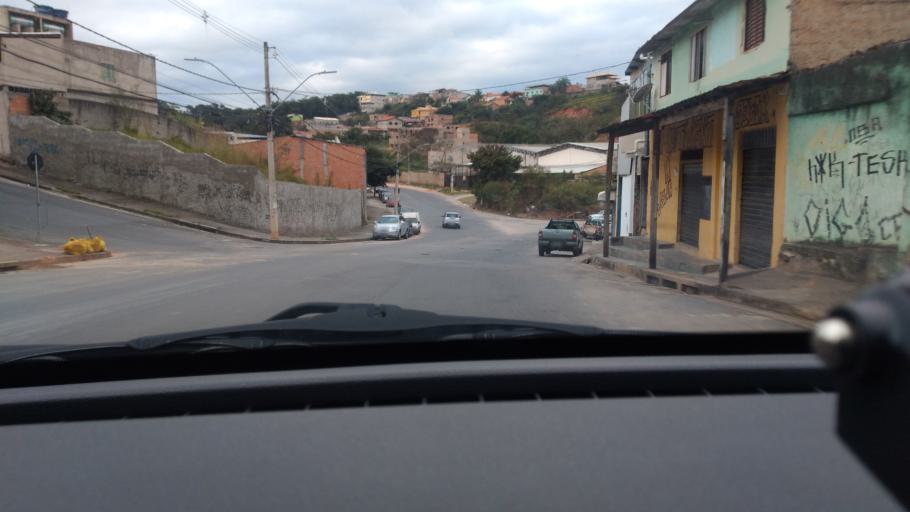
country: BR
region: Minas Gerais
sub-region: Santa Luzia
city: Santa Luzia
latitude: -19.8188
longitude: -43.9379
